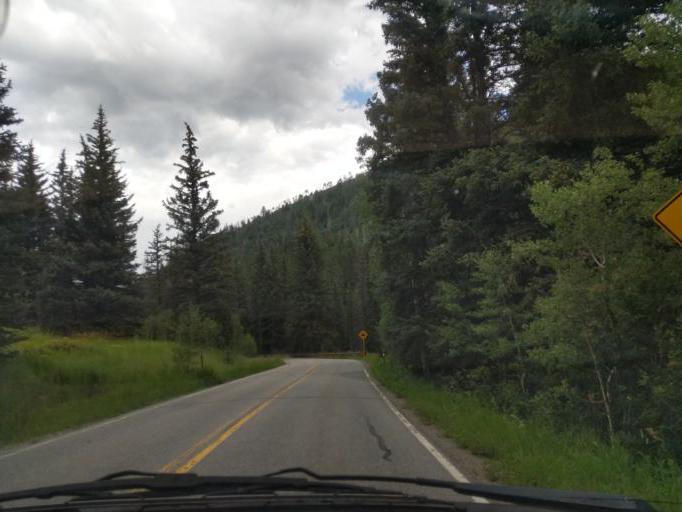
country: US
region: Colorado
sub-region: Garfield County
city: Carbondale
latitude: 39.1037
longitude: -107.2647
